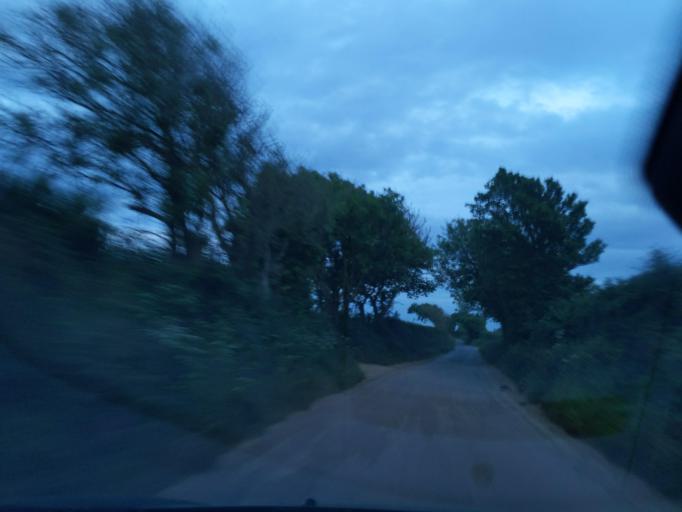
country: GB
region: England
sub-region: Cornwall
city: Wadebridge
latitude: 50.5795
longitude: -4.8324
